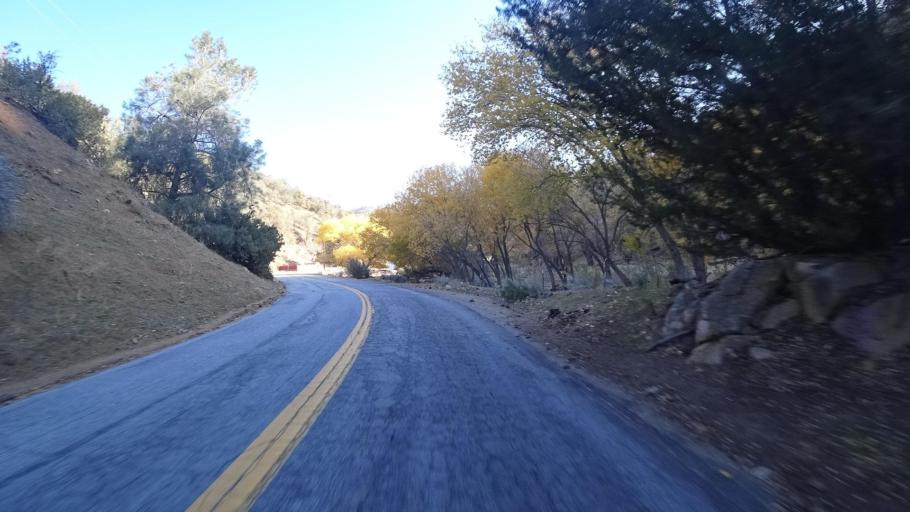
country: US
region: California
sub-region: Kern County
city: Golden Hills
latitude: 35.3036
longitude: -118.4643
